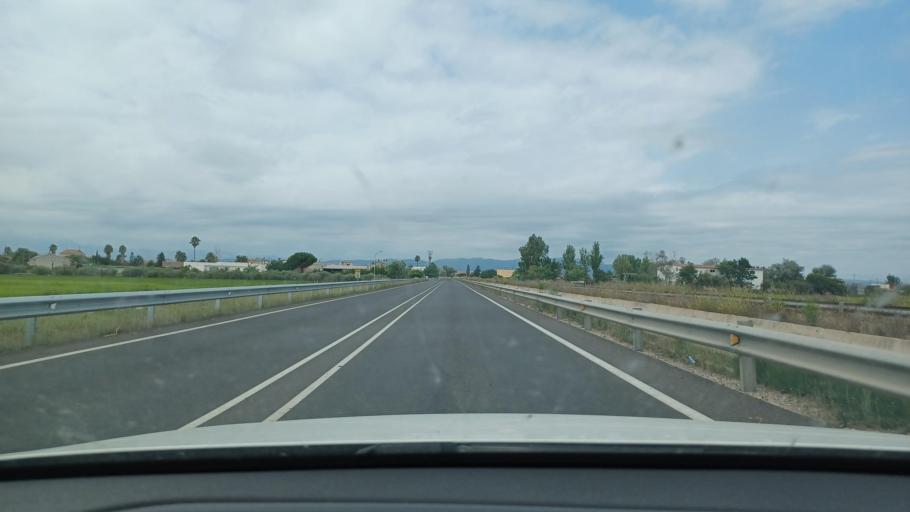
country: ES
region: Catalonia
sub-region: Provincia de Tarragona
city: Deltebre
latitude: 40.7148
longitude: 0.7533
